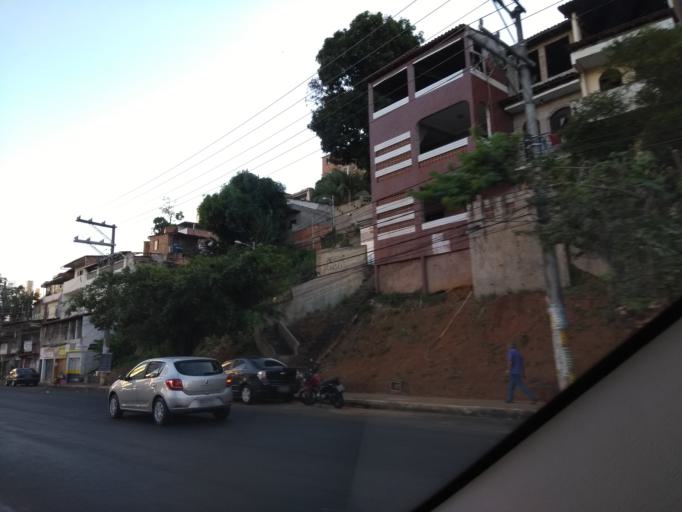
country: BR
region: Bahia
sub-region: Salvador
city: Salvador
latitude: -12.9986
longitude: -38.4923
